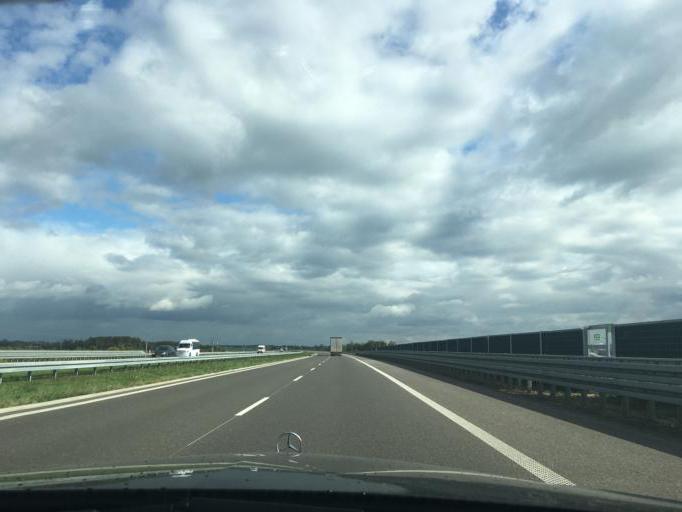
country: PL
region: Subcarpathian Voivodeship
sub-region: Powiat rzeszowski
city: Krasne
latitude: 50.0925
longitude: 22.0739
